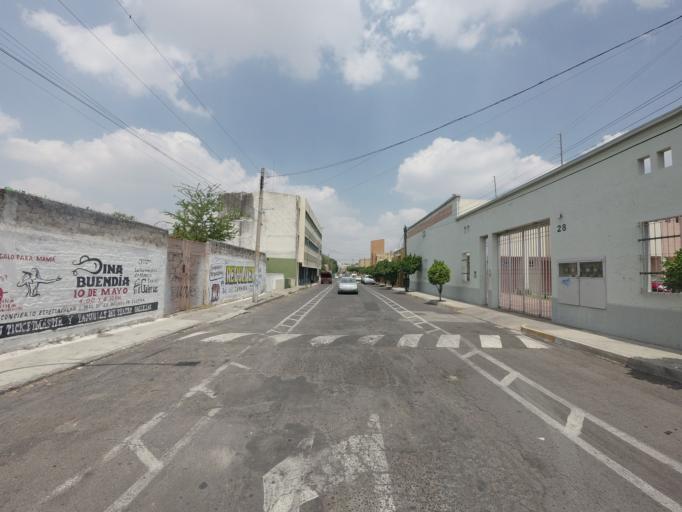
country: MX
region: Jalisco
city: Guadalajara
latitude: 20.6838
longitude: -103.3410
